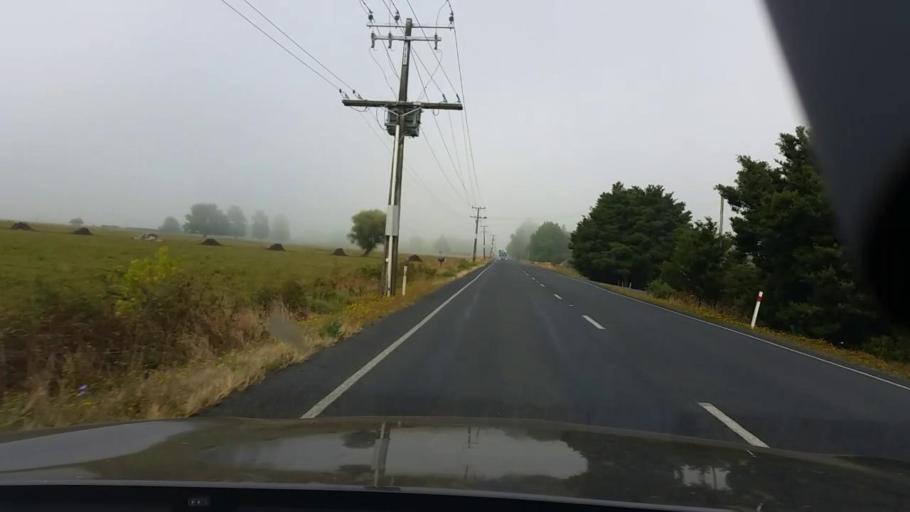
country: NZ
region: Waikato
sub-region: Hamilton City
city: Hamilton
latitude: -37.6284
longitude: 175.3171
